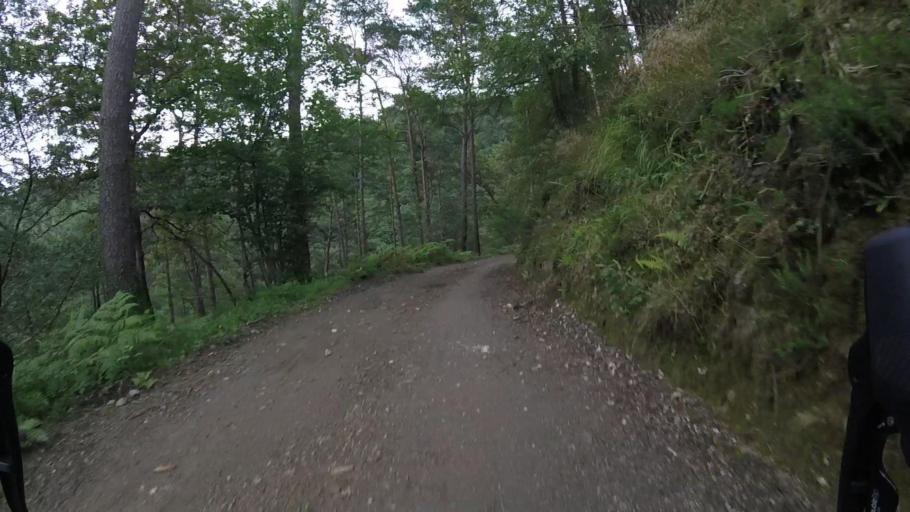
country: ES
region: Navarre
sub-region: Provincia de Navarra
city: Arano
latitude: 43.2545
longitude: -1.8561
